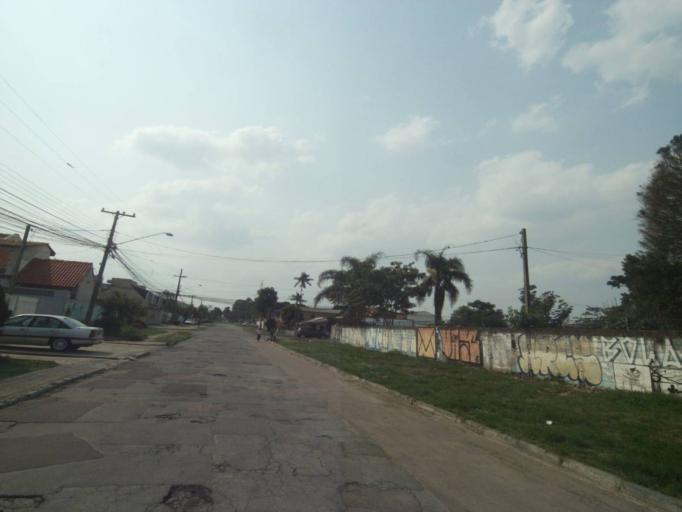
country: BR
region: Parana
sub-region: Sao Jose Dos Pinhais
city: Sao Jose dos Pinhais
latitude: -25.5274
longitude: -49.2303
